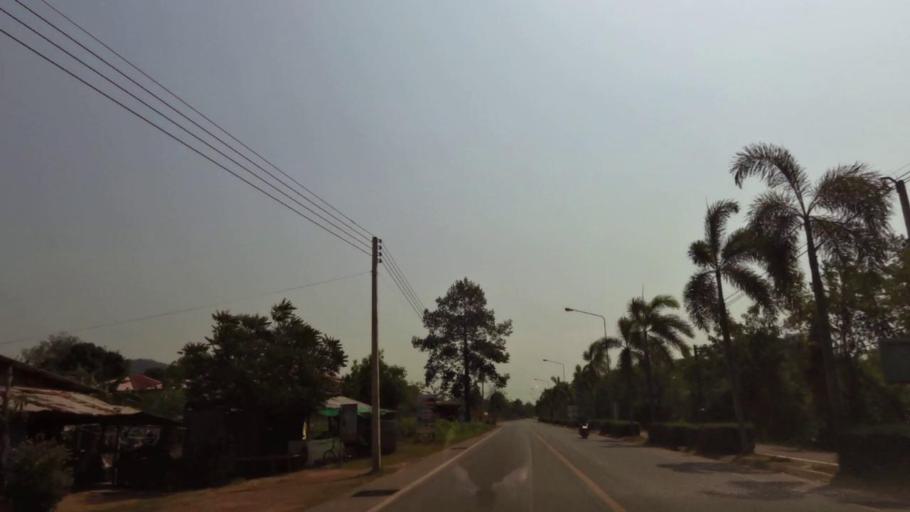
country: TH
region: Chanthaburi
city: Tha Mai
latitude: 12.5492
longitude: 101.9264
